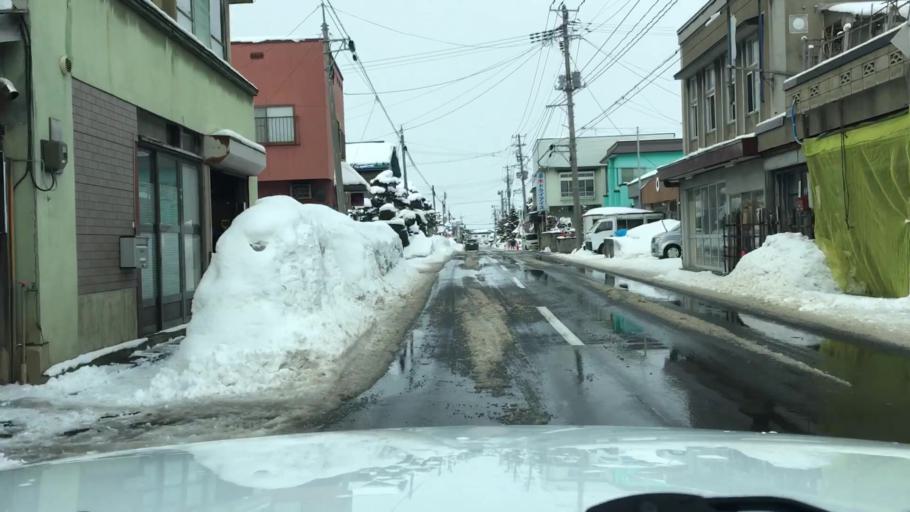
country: JP
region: Aomori
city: Hirosaki
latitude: 40.5793
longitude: 140.4978
